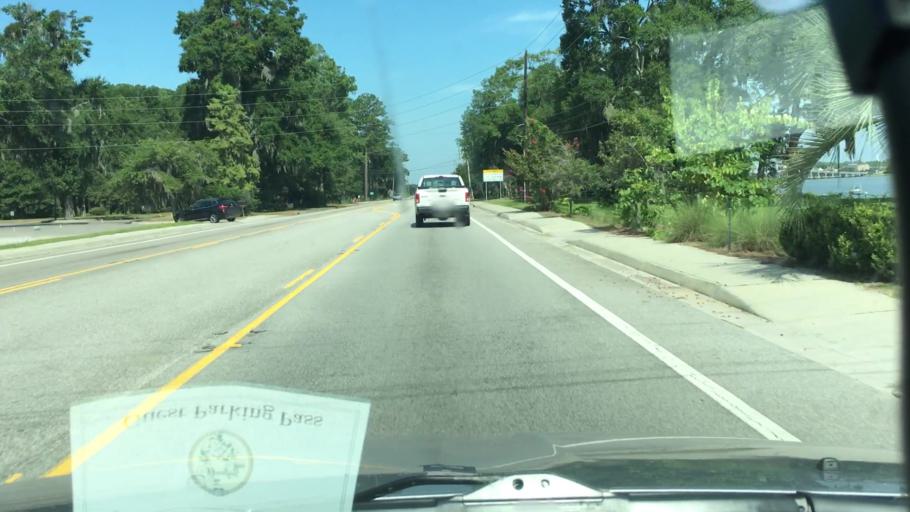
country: US
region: South Carolina
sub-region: Beaufort County
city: Beaufort
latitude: 32.4195
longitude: -80.6614
